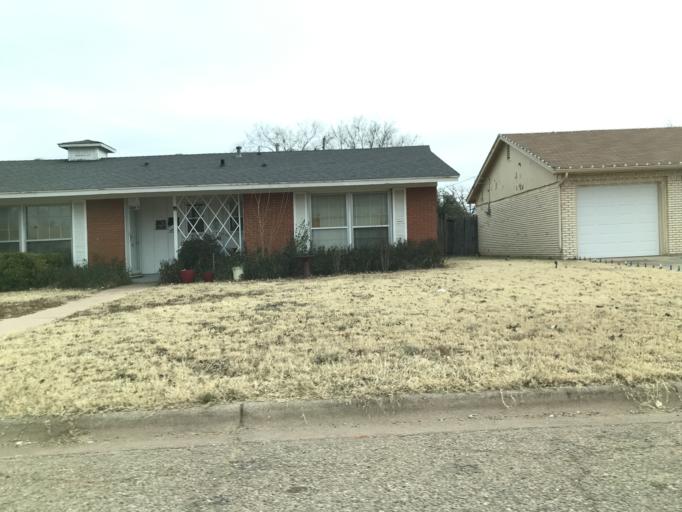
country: US
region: Texas
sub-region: Taylor County
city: Abilene
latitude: 32.4732
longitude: -99.7621
